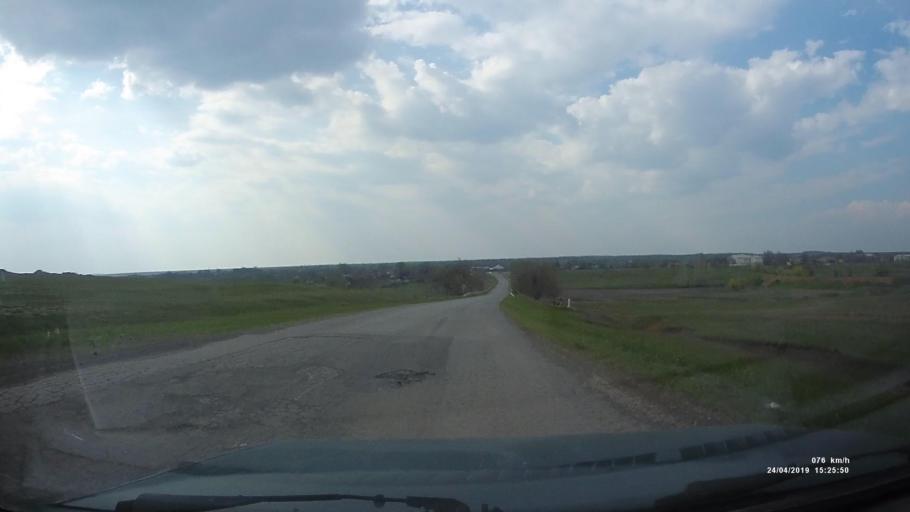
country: RU
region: Rostov
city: Remontnoye
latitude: 46.5544
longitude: 43.0402
